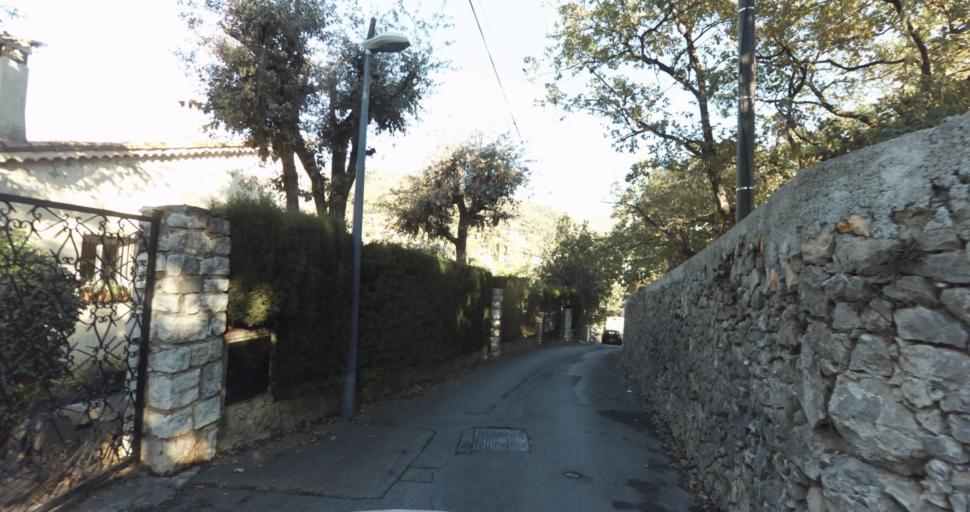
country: FR
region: Provence-Alpes-Cote d'Azur
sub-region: Departement des Alpes-Maritimes
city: Vence
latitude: 43.7223
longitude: 7.1030
